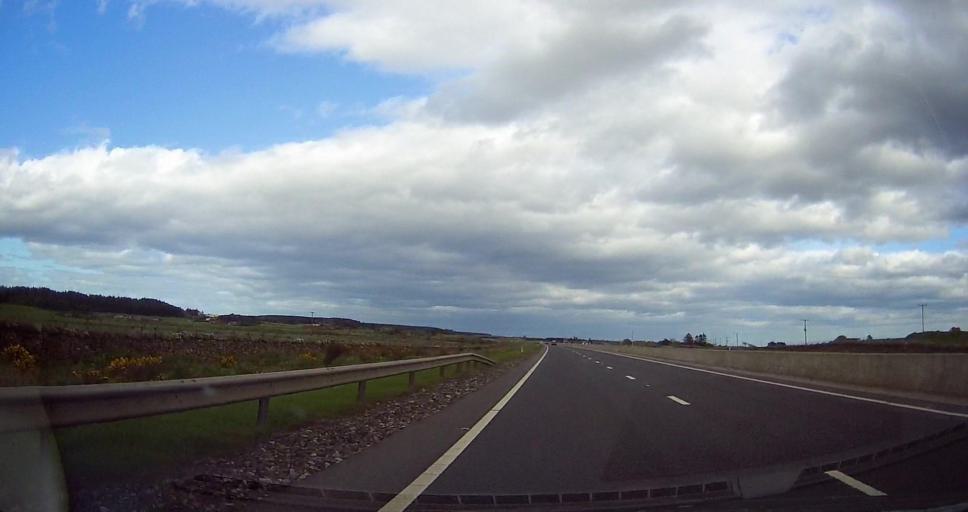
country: GB
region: Scotland
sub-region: Aberdeen City
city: Cults
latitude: 57.0814
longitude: -2.1645
